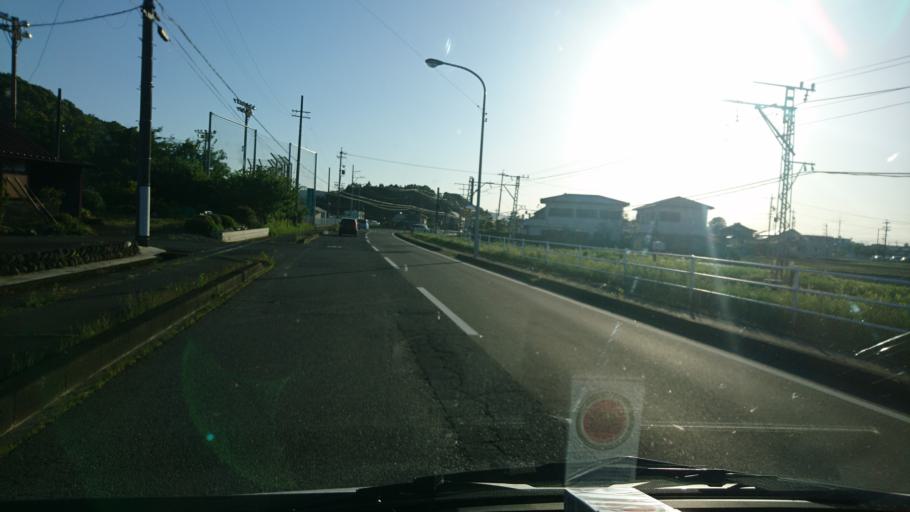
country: JP
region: Gifu
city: Mitake
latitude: 35.4260
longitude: 137.0730
